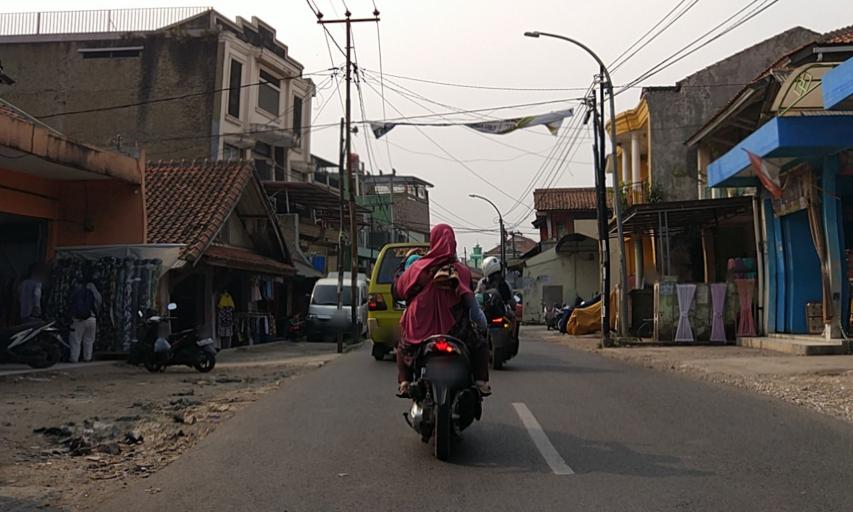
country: ID
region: West Java
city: Margahayukencana
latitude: -6.9462
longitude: 107.5647
